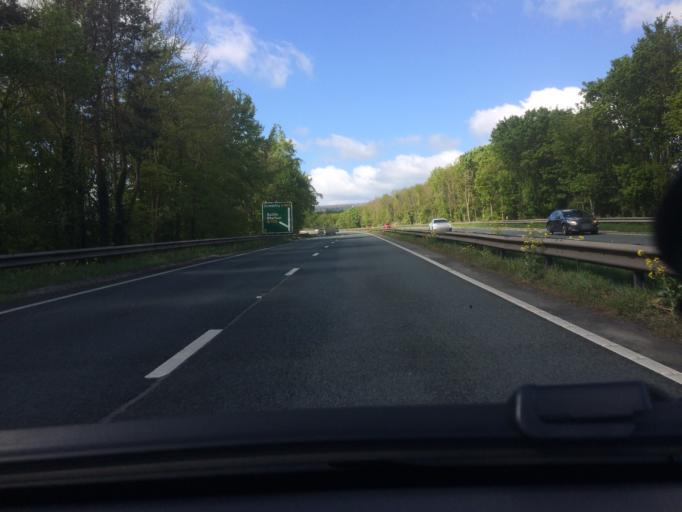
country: GB
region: Wales
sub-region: Wrexham
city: Wrexham
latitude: 53.0485
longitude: -3.0207
